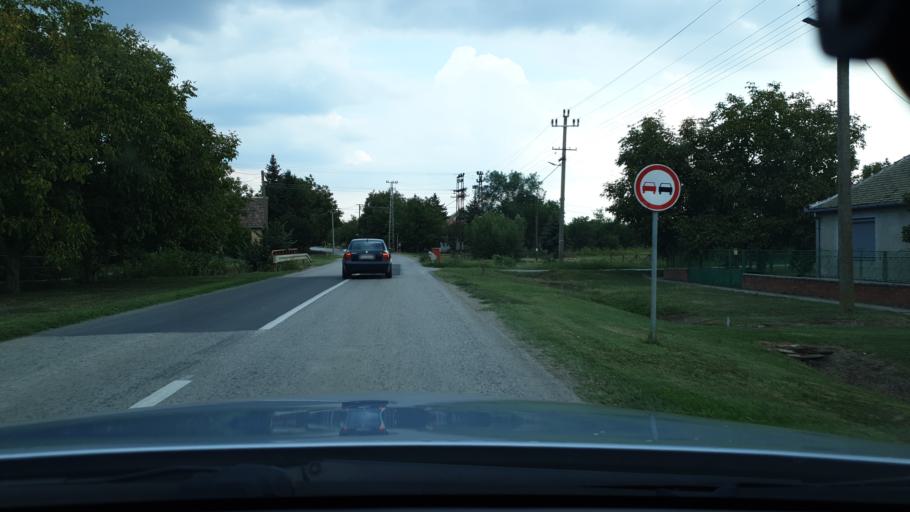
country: RS
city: Konak
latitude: 45.3162
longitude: 20.9078
